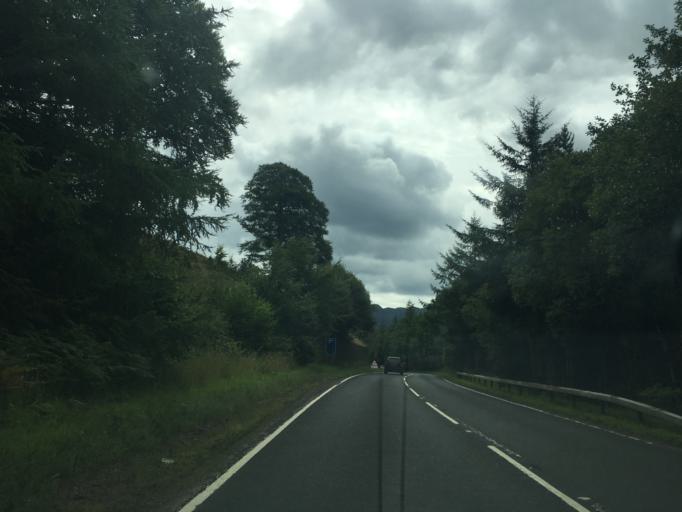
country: GB
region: Scotland
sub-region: Stirling
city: Callander
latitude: 56.3395
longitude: -4.3256
